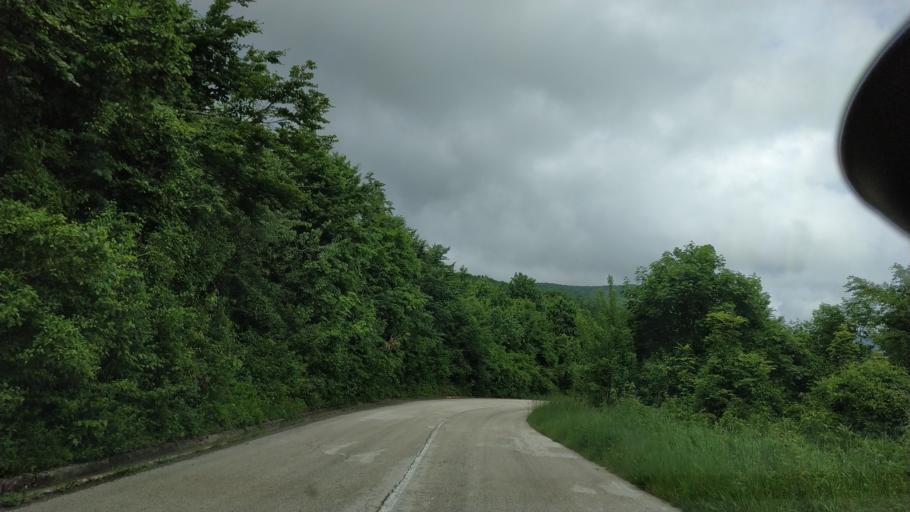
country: RS
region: Central Serbia
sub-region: Zajecarski Okrug
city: Boljevac
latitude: 43.7257
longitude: 21.9527
